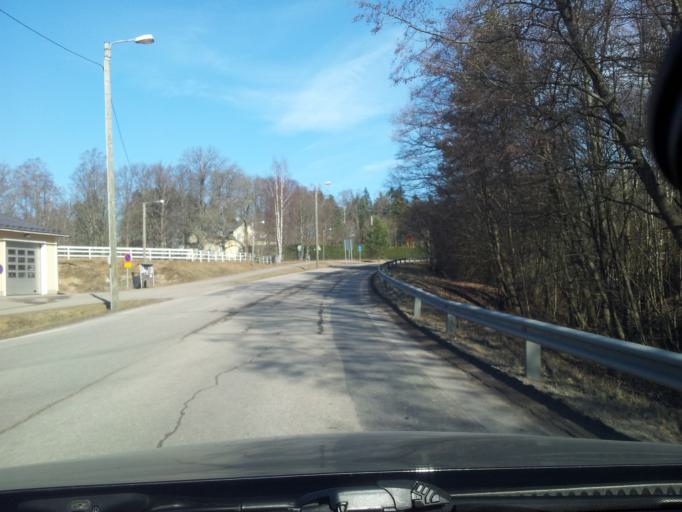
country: FI
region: Uusimaa
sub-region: Helsinki
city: Espoo
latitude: 60.1794
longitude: 24.5480
